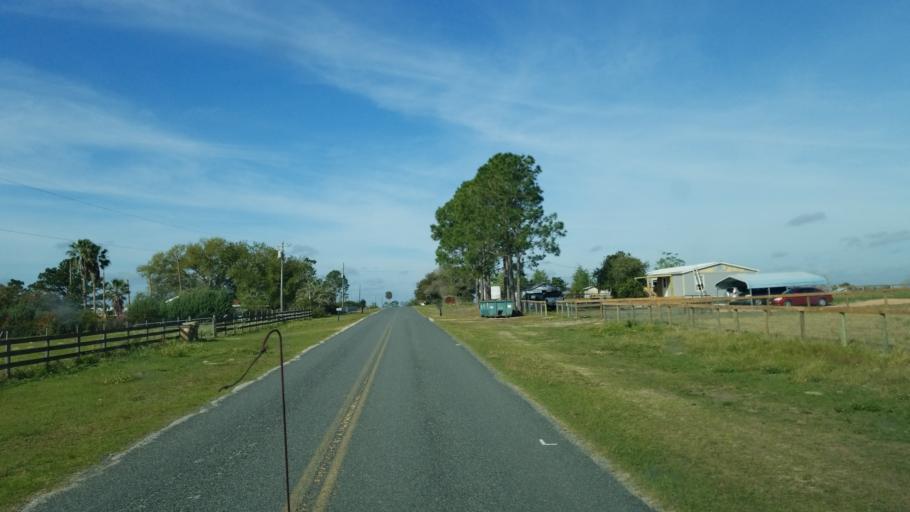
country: US
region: Florida
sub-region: Lake County
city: Clermont
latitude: 28.4451
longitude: -81.7958
